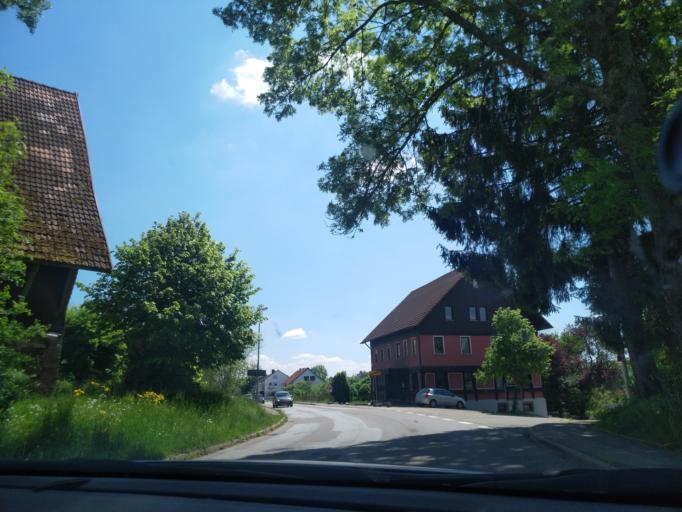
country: DE
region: Baden-Wuerttemberg
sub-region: Freiburg Region
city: Dornhan
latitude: 48.3276
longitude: 8.4642
